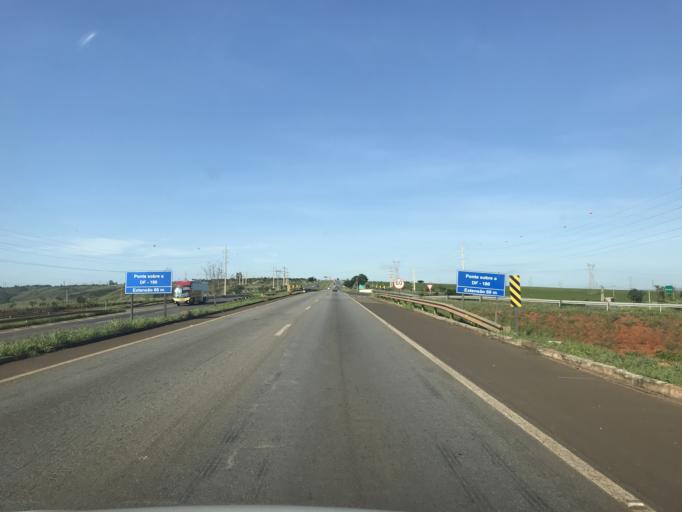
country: BR
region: Federal District
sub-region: Brasilia
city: Brasilia
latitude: -15.9074
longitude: -48.1435
